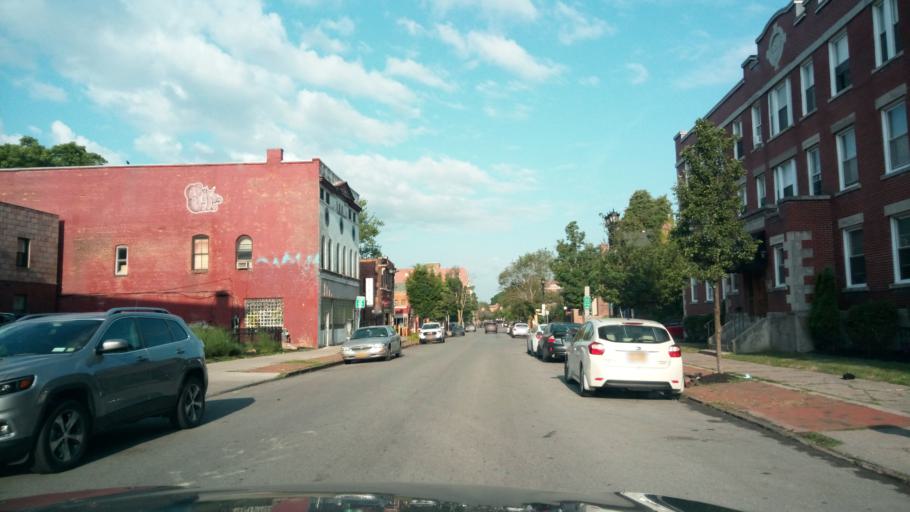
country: US
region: New York
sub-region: Erie County
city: Buffalo
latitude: 42.8994
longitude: -78.8745
